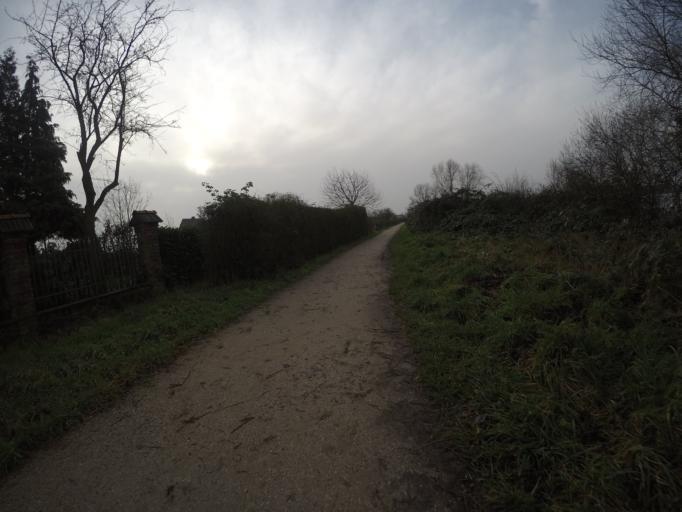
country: DE
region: North Rhine-Westphalia
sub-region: Regierungsbezirk Dusseldorf
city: Xanten
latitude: 51.6749
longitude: 6.4532
